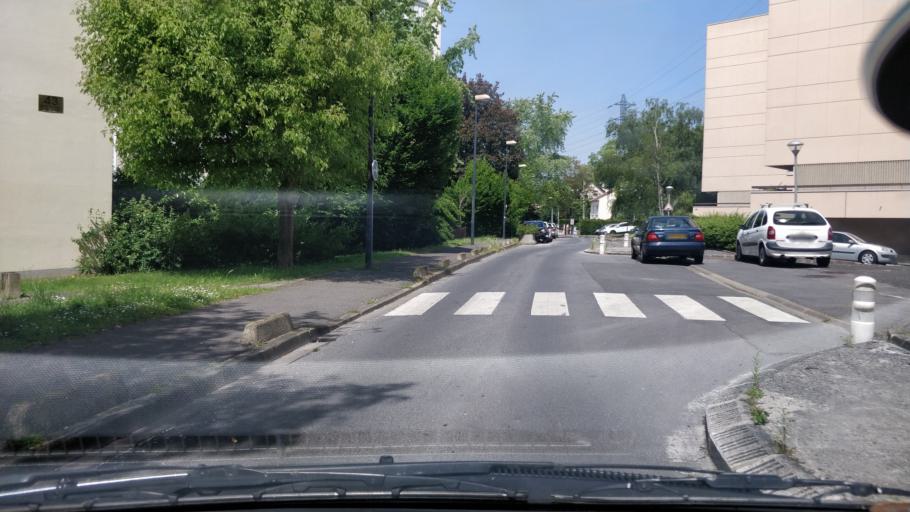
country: FR
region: Ile-de-France
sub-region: Departement de Seine-et-Marne
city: Chelles
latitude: 48.8819
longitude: 2.5925
